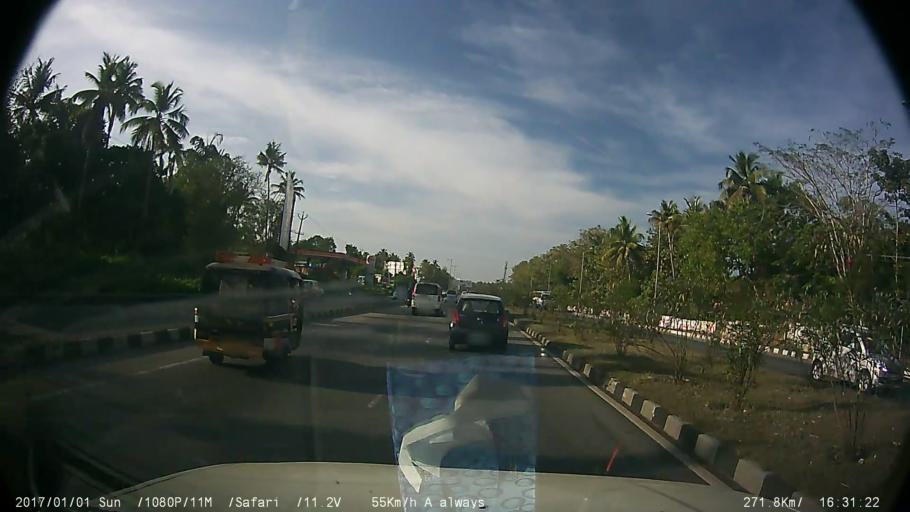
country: IN
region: Kerala
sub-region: Thrissur District
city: Kizhake Chalakudi
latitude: 10.3203
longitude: 76.3261
